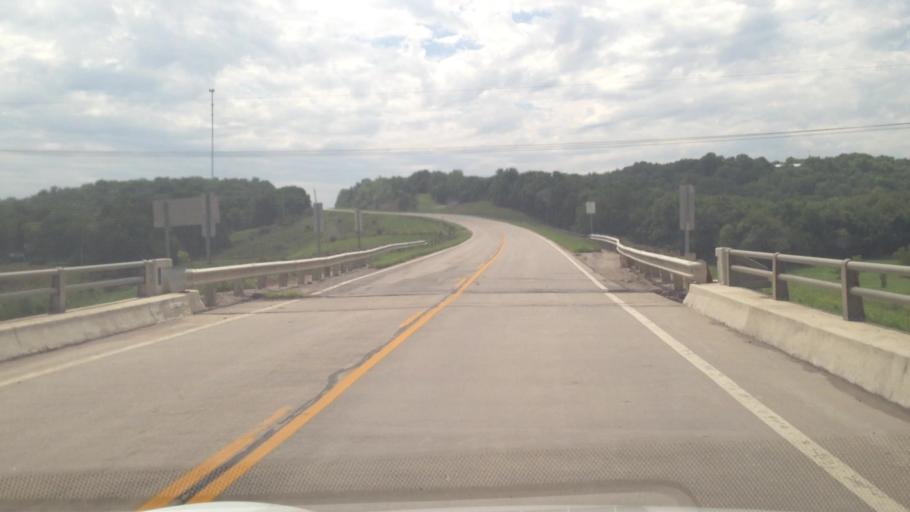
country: US
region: Kansas
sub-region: Bourbon County
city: Fort Scott
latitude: 37.8350
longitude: -94.9813
